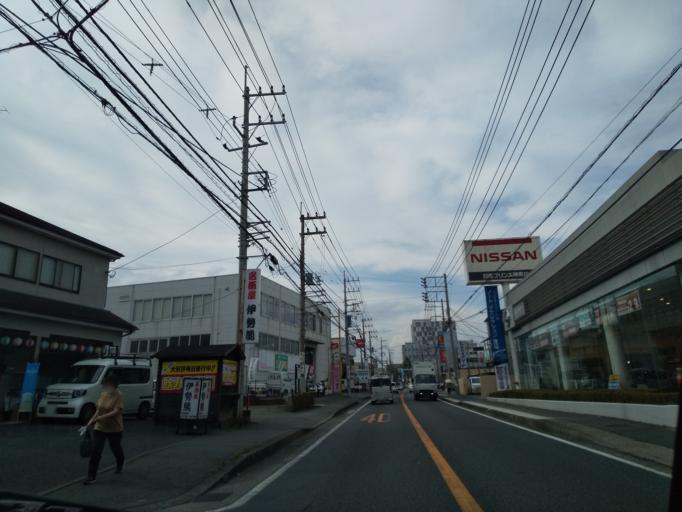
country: JP
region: Kanagawa
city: Atsugi
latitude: 35.4820
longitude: 139.3414
